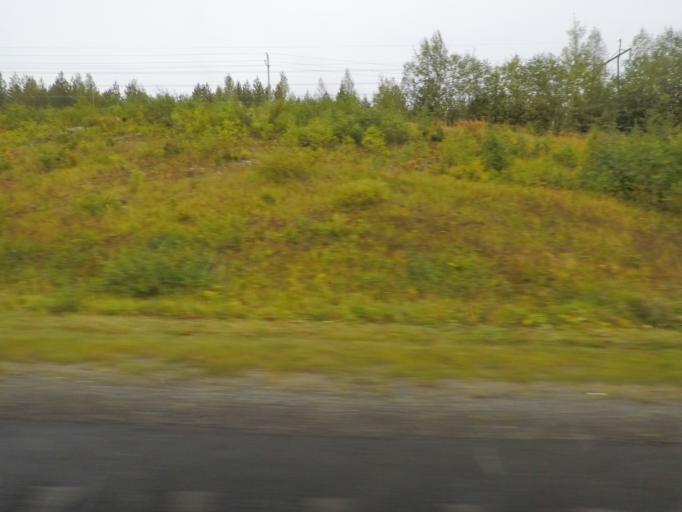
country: FI
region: Northern Savo
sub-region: Kuopio
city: Kuopio
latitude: 62.7057
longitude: 27.5685
